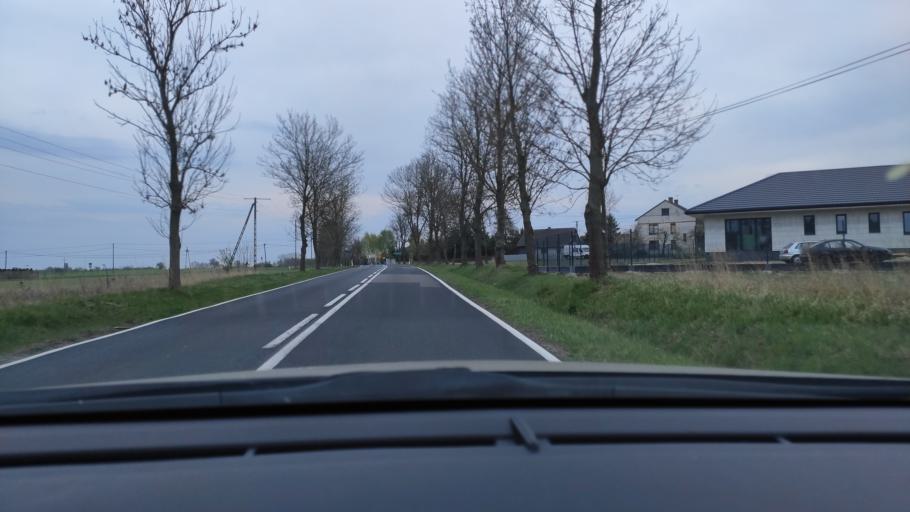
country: PL
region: Masovian Voivodeship
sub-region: Powiat zwolenski
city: Zwolen
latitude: 51.3843
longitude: 21.5563
